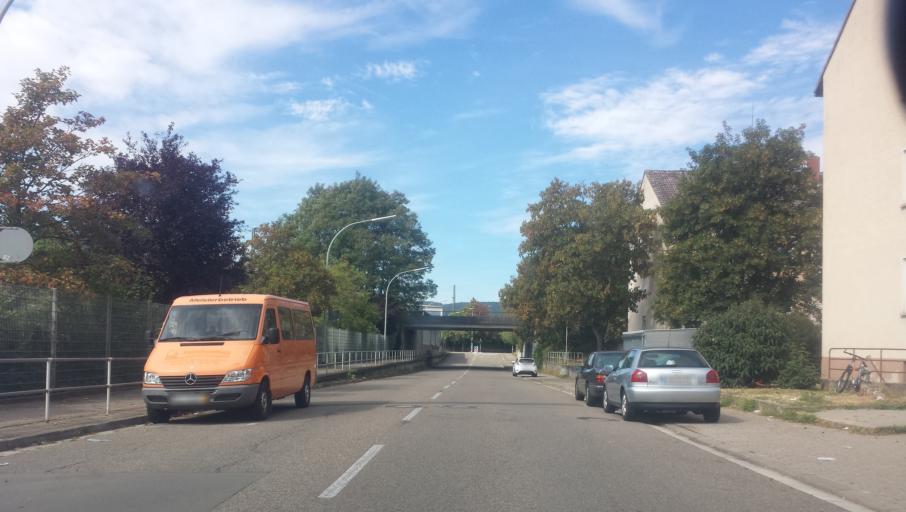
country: DE
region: Rheinland-Pfalz
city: Neustadt
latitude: 49.3494
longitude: 8.1547
